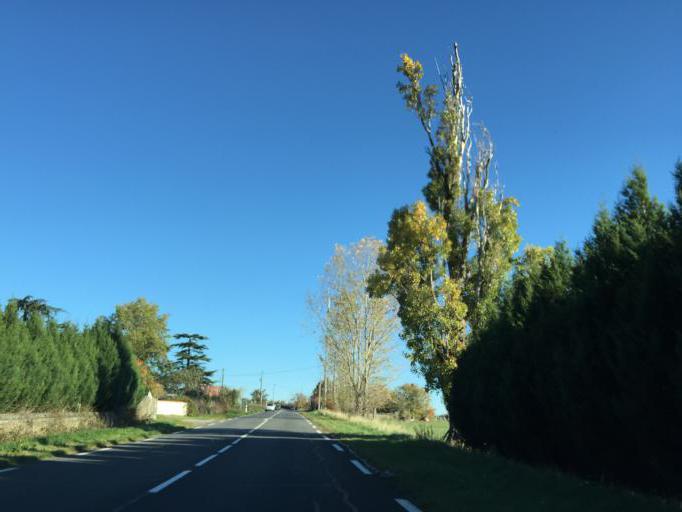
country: FR
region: Rhone-Alpes
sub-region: Departement du Rhone
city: Saint-Maurice-sur-Dargoire
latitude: 45.5678
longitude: 4.6442
